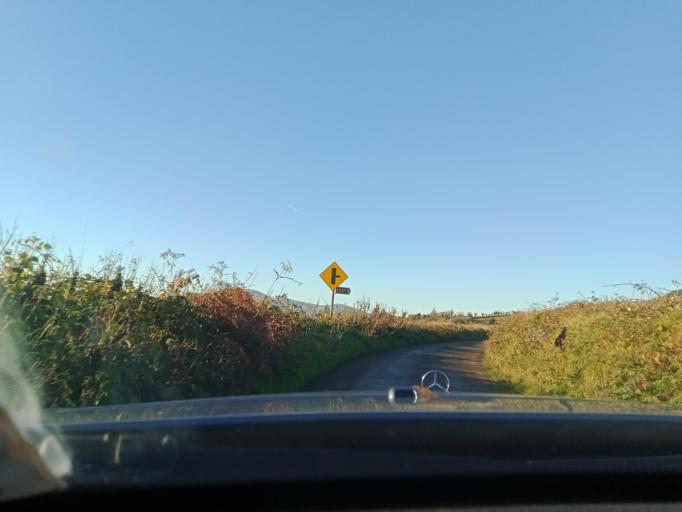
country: IE
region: Leinster
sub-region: Kilkenny
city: Callan
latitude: 52.4609
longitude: -7.4186
